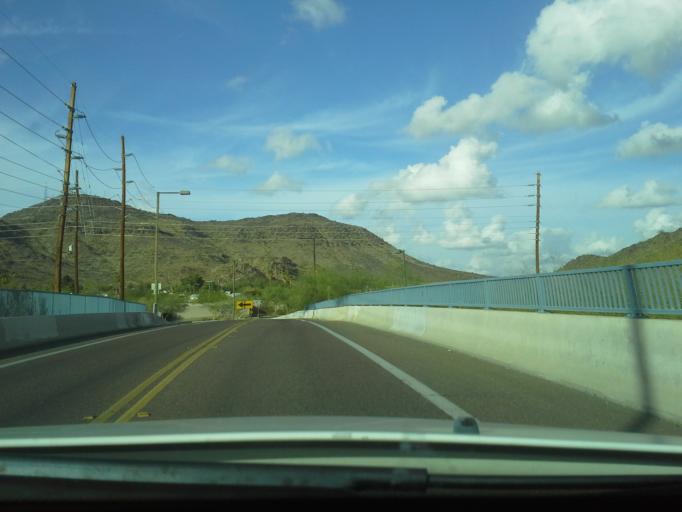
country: US
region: Arizona
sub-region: Maricopa County
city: Glendale
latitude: 33.5814
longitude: -112.0826
